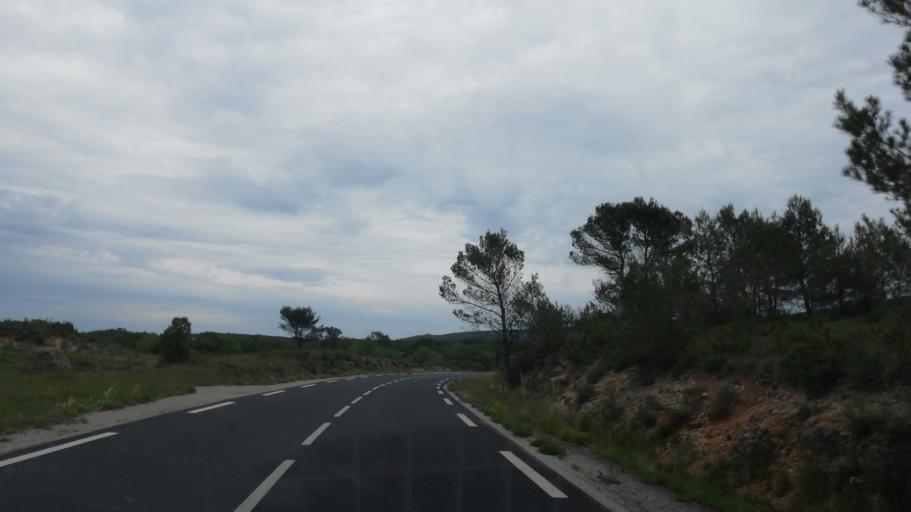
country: FR
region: Languedoc-Roussillon
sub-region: Departement de l'Herault
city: Saint-Martin-de-Londres
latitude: 43.7926
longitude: 3.7964
